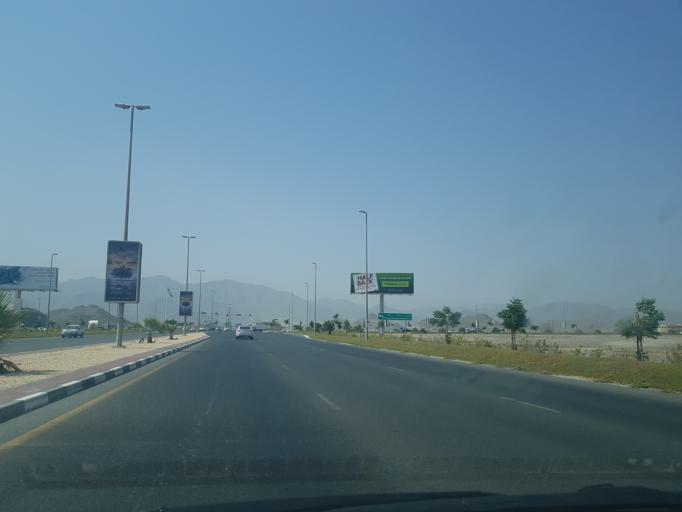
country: AE
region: Al Fujayrah
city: Al Fujayrah
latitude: 25.1225
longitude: 56.2990
